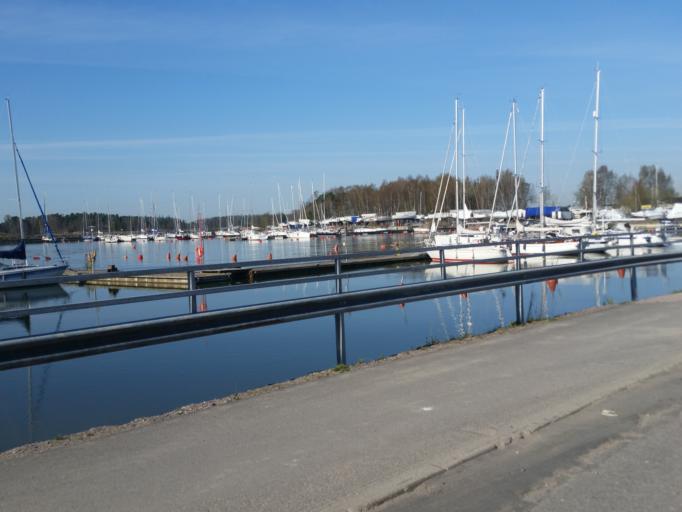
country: FI
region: Uusimaa
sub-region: Helsinki
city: Teekkarikylae
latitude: 60.1632
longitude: 24.8551
